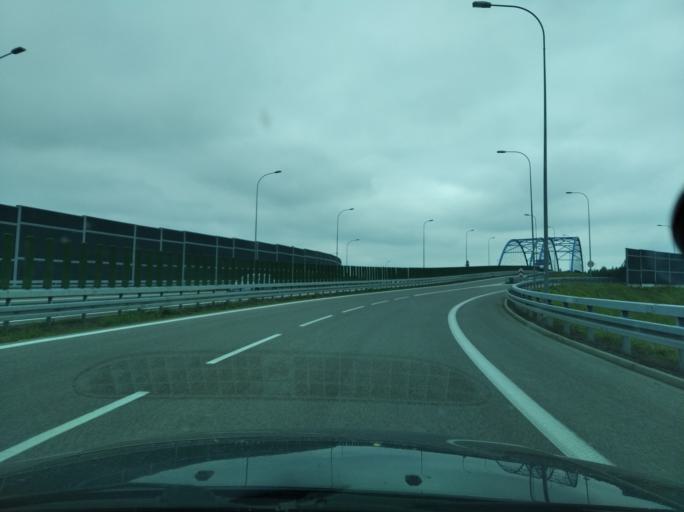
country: PL
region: Subcarpathian Voivodeship
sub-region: Powiat ropczycko-sedziszowski
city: Sedziszow Malopolski
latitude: 50.1072
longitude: 21.6646
